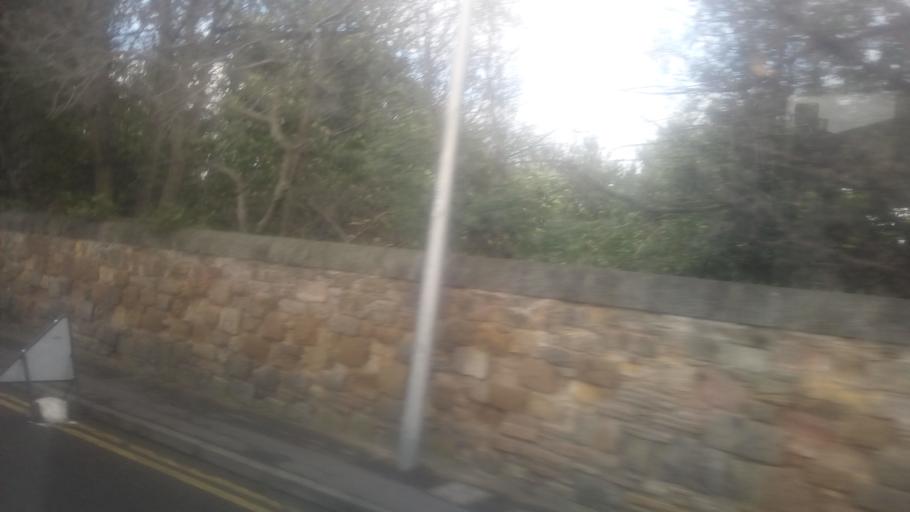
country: GB
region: Scotland
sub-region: Midlothian
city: Dalkeith
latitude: 55.8951
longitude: -3.0707
